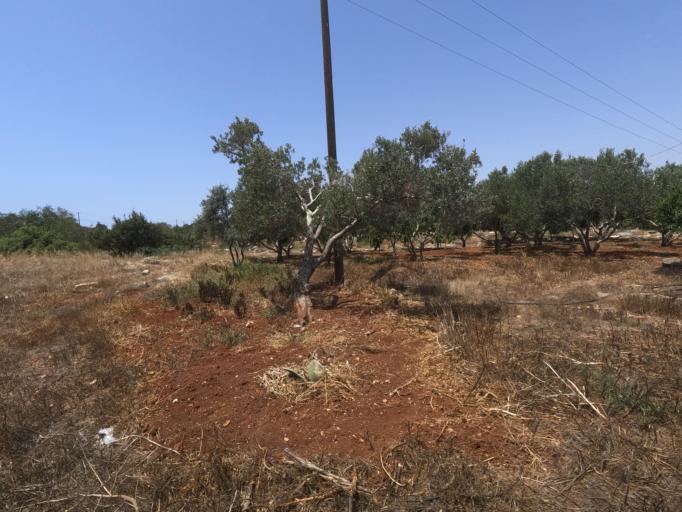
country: CY
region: Ammochostos
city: Ayia Napa
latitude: 35.0064
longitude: 33.9953
